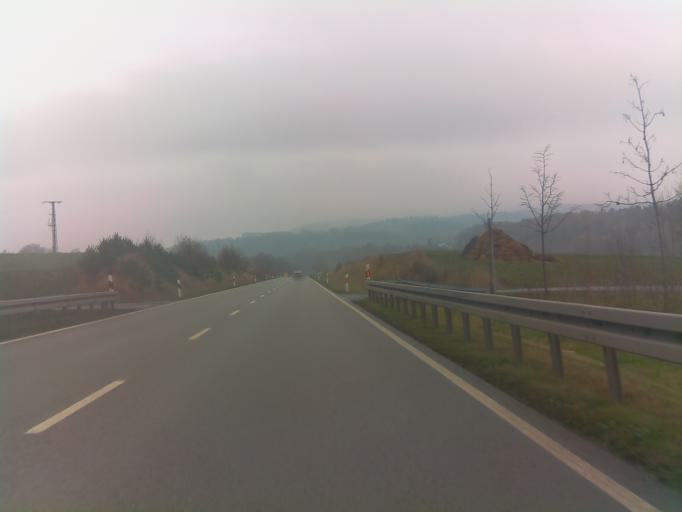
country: DE
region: Thuringia
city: Schleusingen
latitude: 50.4950
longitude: 10.7681
